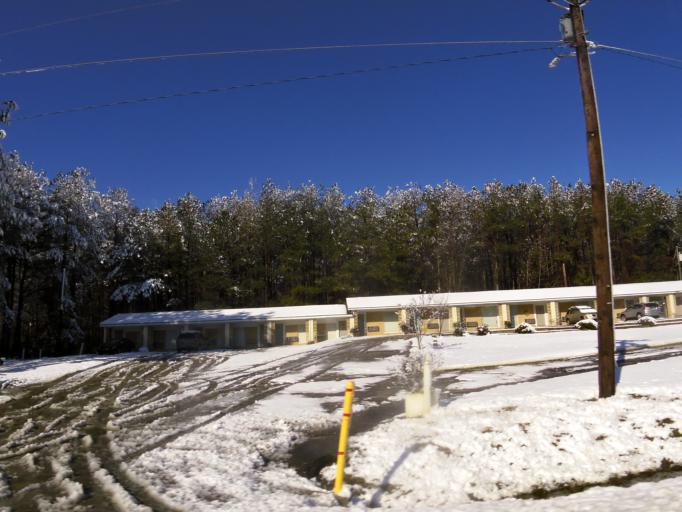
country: US
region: North Carolina
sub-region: Nash County
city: Sharpsburg
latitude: 35.8785
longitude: -77.8243
